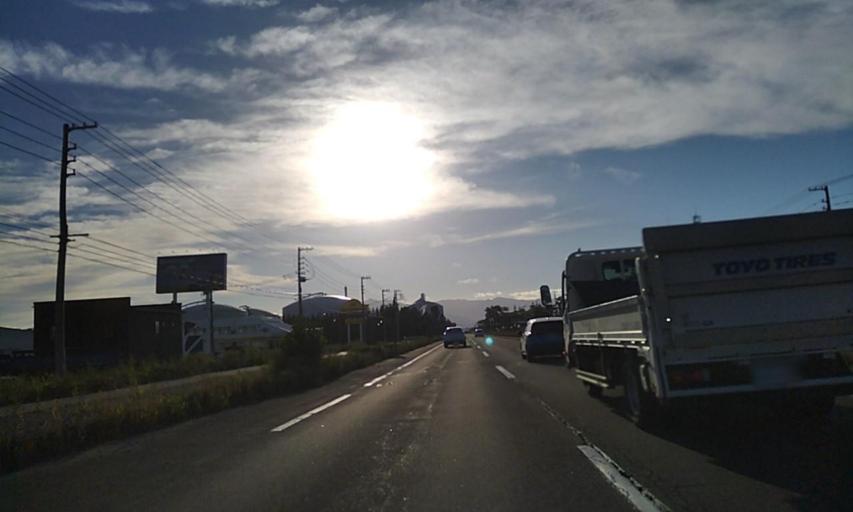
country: JP
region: Hokkaido
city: Obihiro
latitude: 42.9235
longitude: 143.0876
